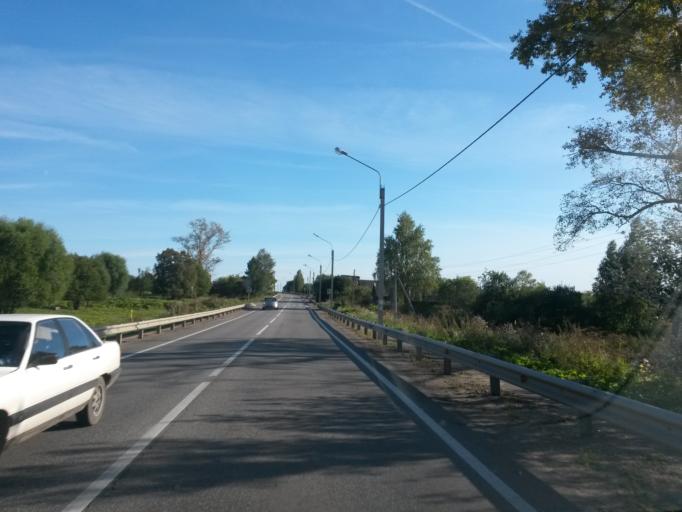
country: RU
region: Jaroslavl
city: Gavrilov-Yam
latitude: 57.3510
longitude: 39.9086
